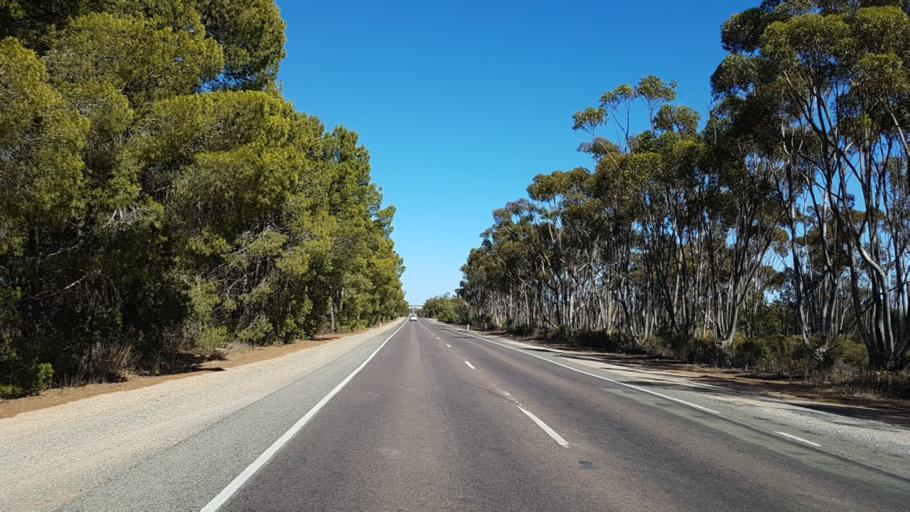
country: AU
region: South Australia
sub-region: Copper Coast
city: Kadina
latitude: -34.0575
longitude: 138.0233
